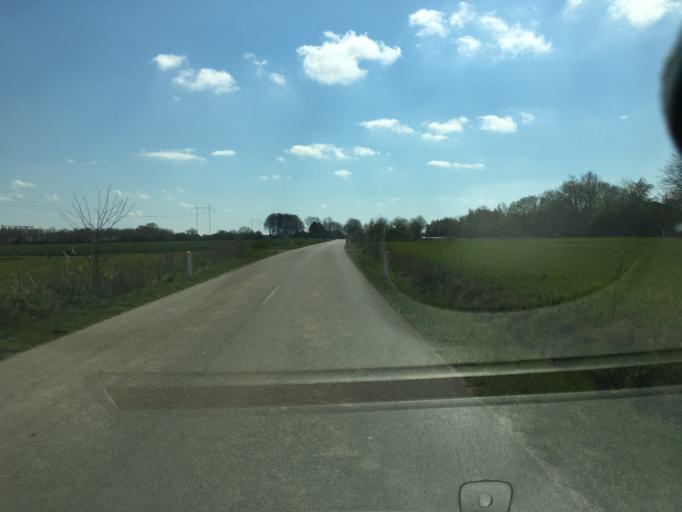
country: DK
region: South Denmark
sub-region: Sonderborg Kommune
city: Dybbol
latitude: 54.9541
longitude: 9.7042
